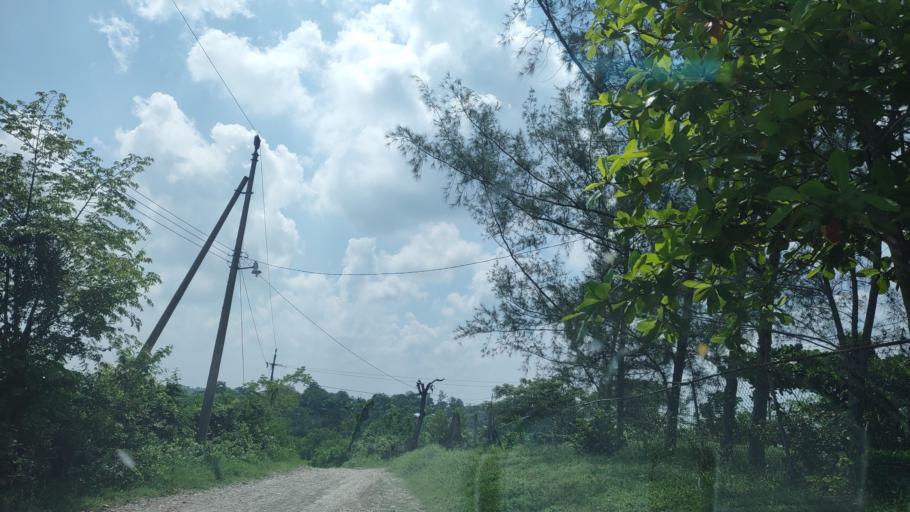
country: MX
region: Veracruz
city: Tempoal de Sanchez
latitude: 21.5525
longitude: -98.2758
